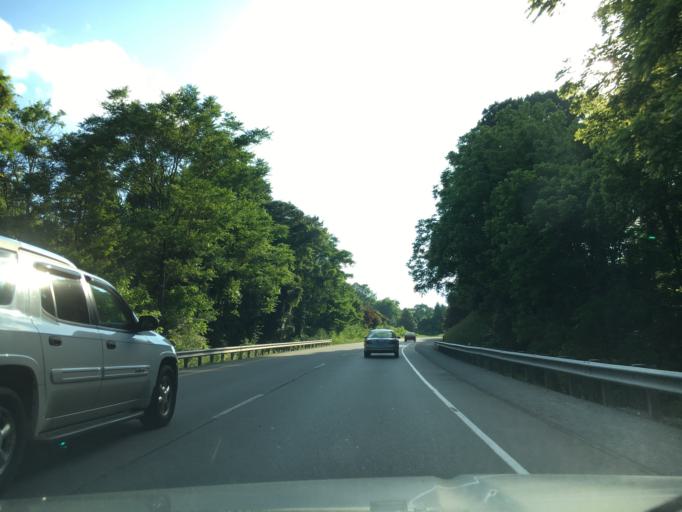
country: US
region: Virginia
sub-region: City of Lynchburg
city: West Lynchburg
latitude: 37.3627
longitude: -79.1885
